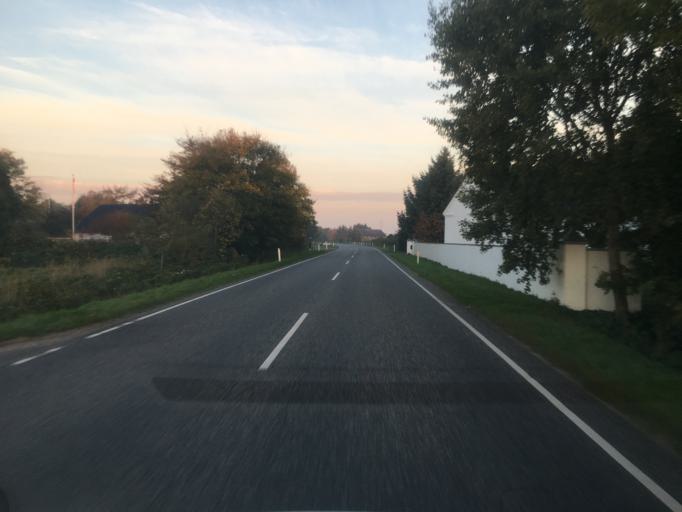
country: DK
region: South Denmark
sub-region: Tonder Kommune
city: Logumkloster
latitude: 55.0326
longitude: 9.0466
